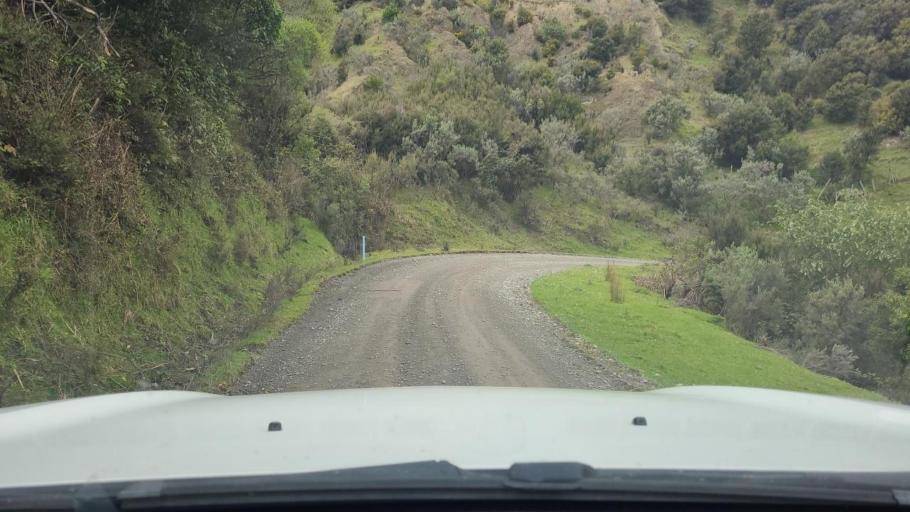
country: NZ
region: Wellington
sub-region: South Wairarapa District
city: Waipawa
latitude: -41.3880
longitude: 175.3737
